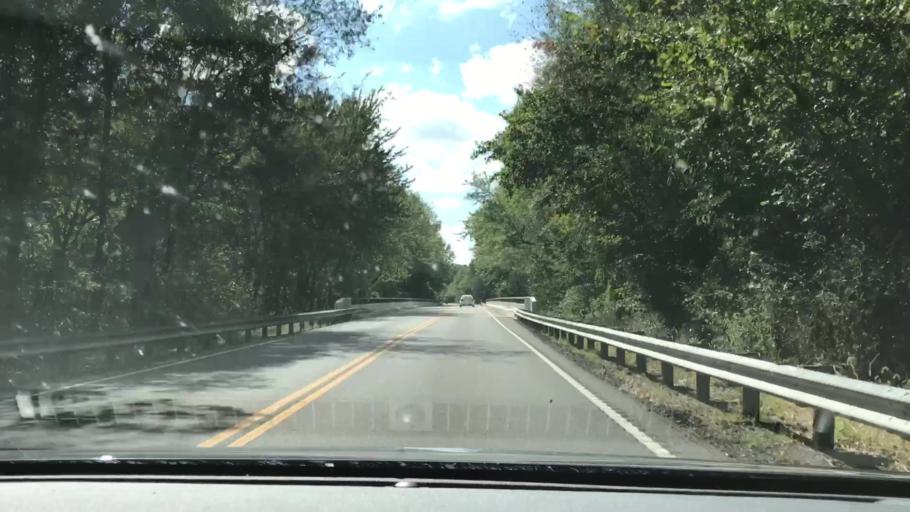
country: US
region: Kentucky
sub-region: McCracken County
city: Reidland
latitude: 36.9726
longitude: -88.5149
